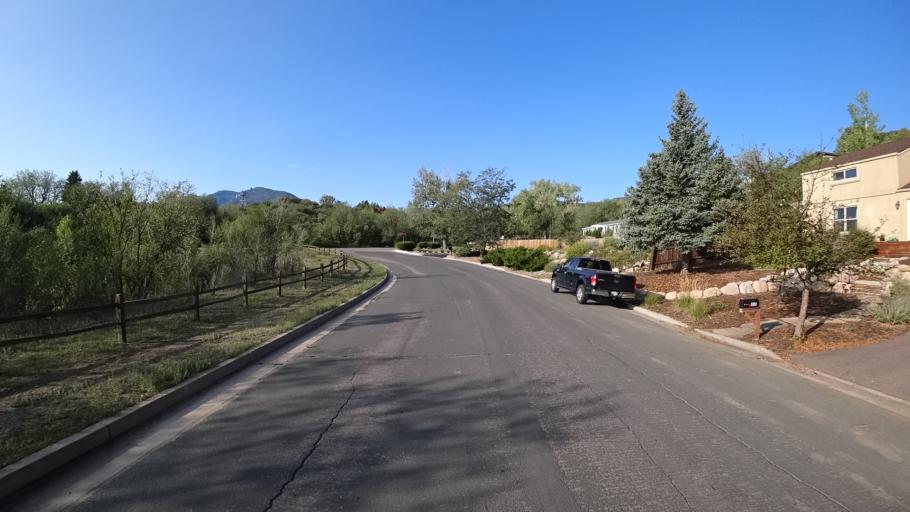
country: US
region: Colorado
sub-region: El Paso County
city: Colorado Springs
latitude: 38.8145
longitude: -104.8527
